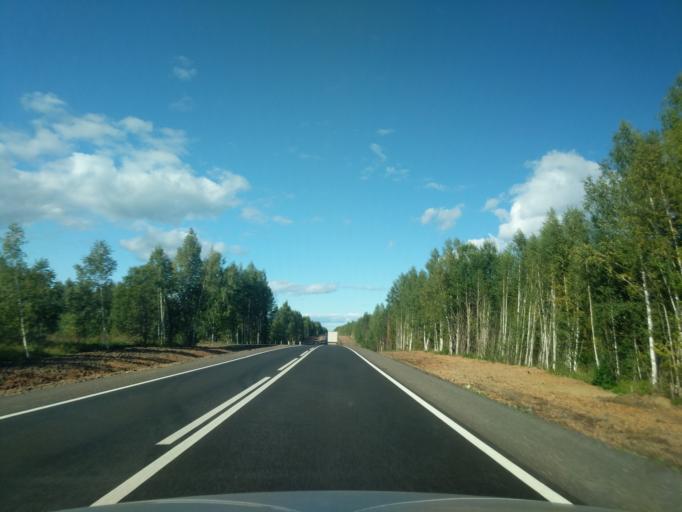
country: RU
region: Kostroma
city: Makar'yev
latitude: 57.9842
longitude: 43.9607
